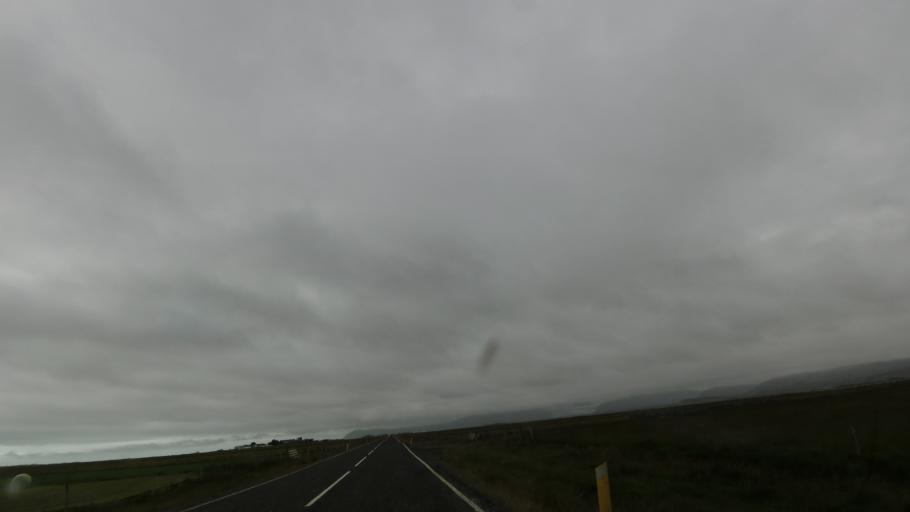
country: IS
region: East
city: Hoefn
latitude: 64.2981
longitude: -15.4246
